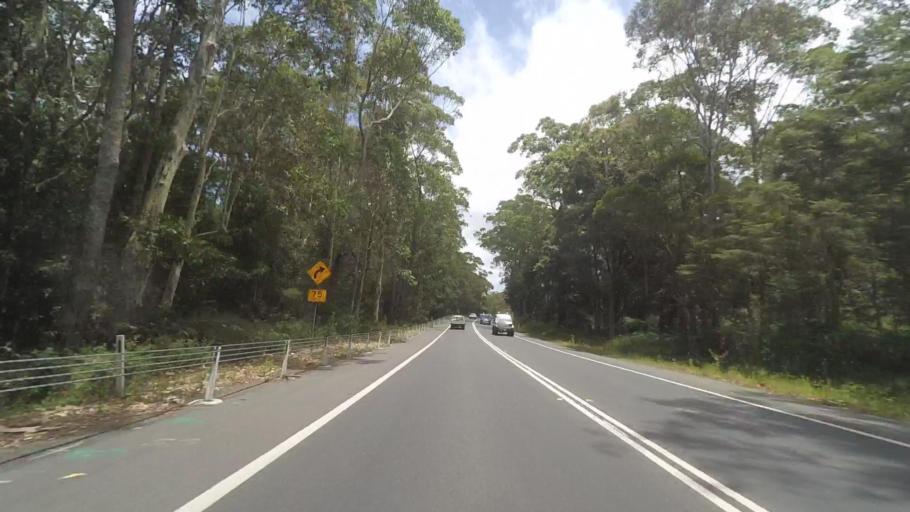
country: AU
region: New South Wales
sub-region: Shoalhaven Shire
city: Falls Creek
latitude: -35.0846
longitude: 150.5412
